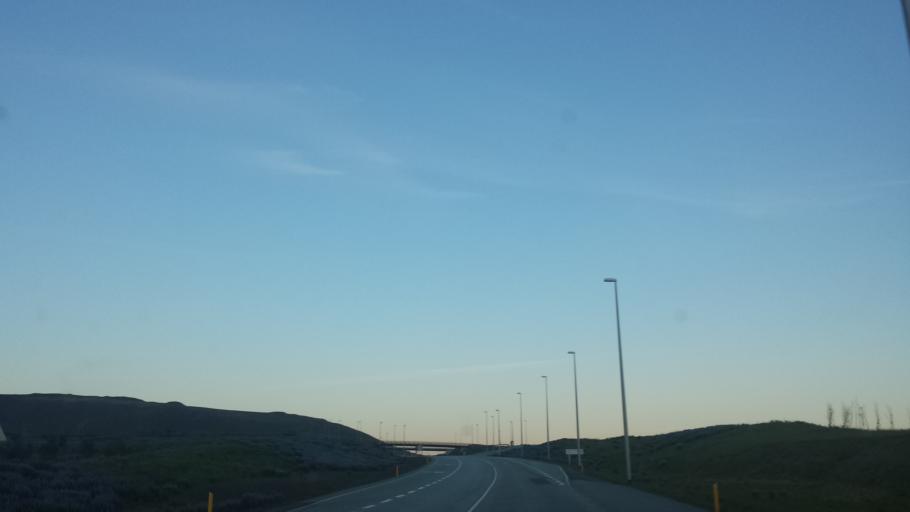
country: IS
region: Capital Region
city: Mosfellsbaer
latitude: 64.1873
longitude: -21.6849
